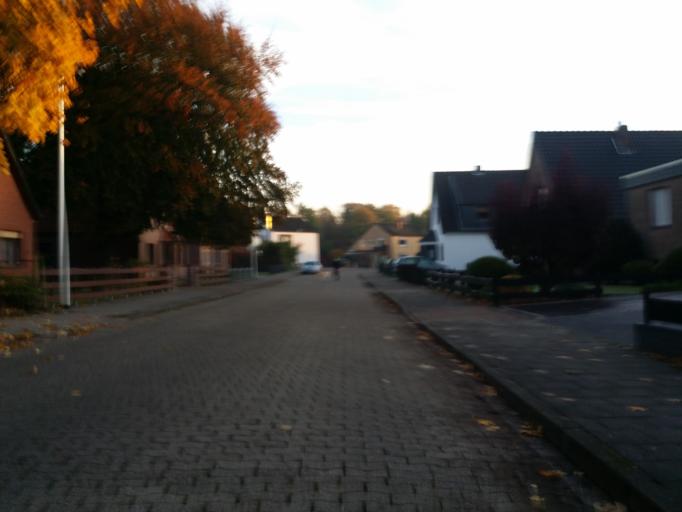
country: DE
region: Lower Saxony
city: Delmenhorst
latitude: 53.0306
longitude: 8.6471
